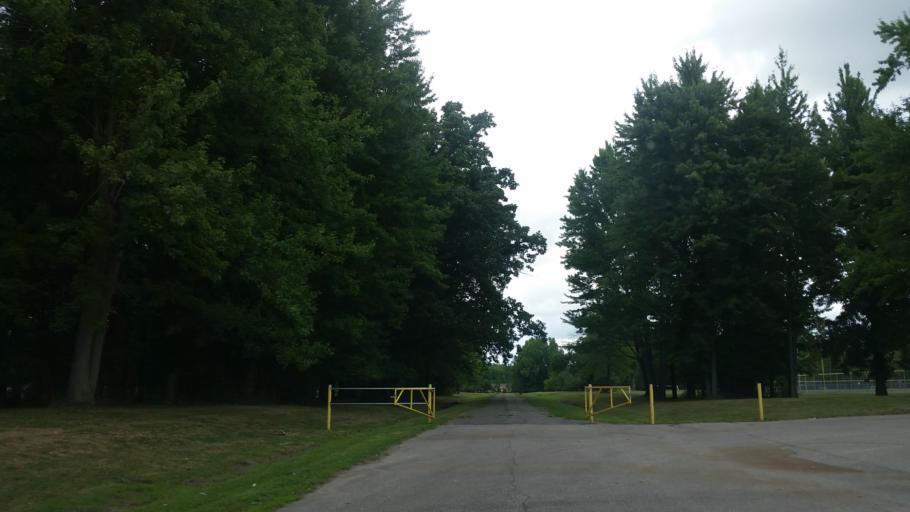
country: US
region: Ohio
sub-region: Cuyahoga County
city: Parma Heights
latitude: 41.3661
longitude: -81.7746
